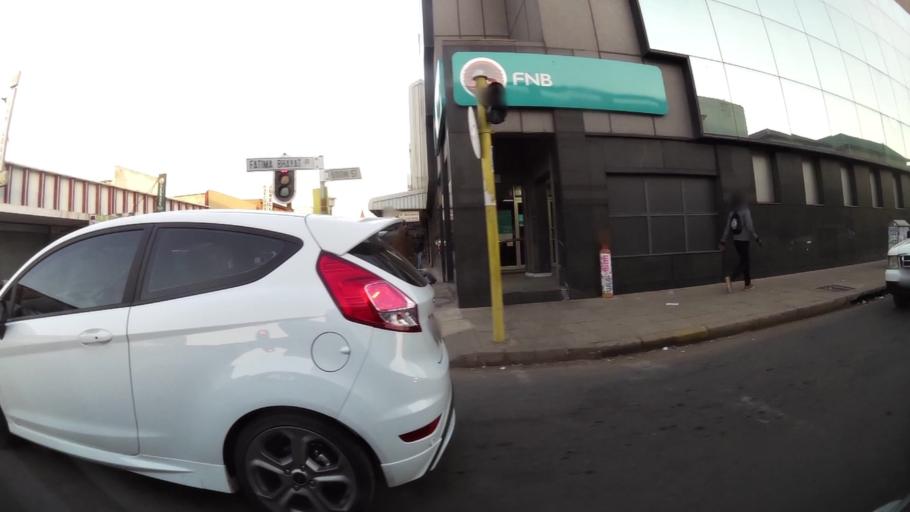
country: ZA
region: North-West
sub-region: Bojanala Platinum District Municipality
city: Rustenburg
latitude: -25.6700
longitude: 27.2433
